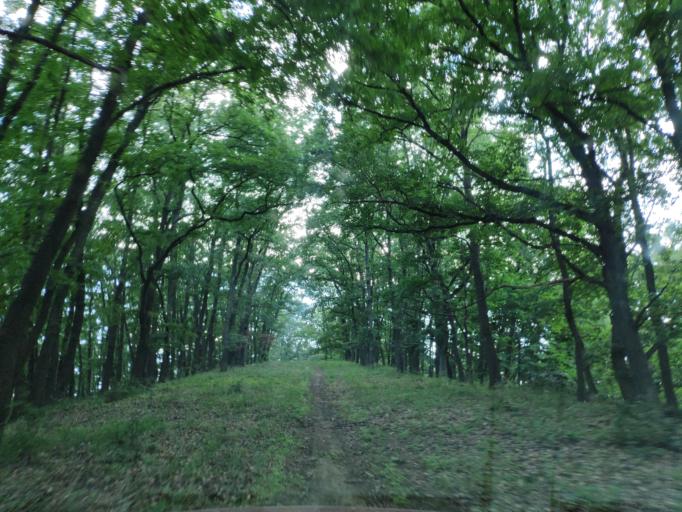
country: HU
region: Borsod-Abauj-Zemplen
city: Arlo
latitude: 48.2544
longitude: 20.1397
